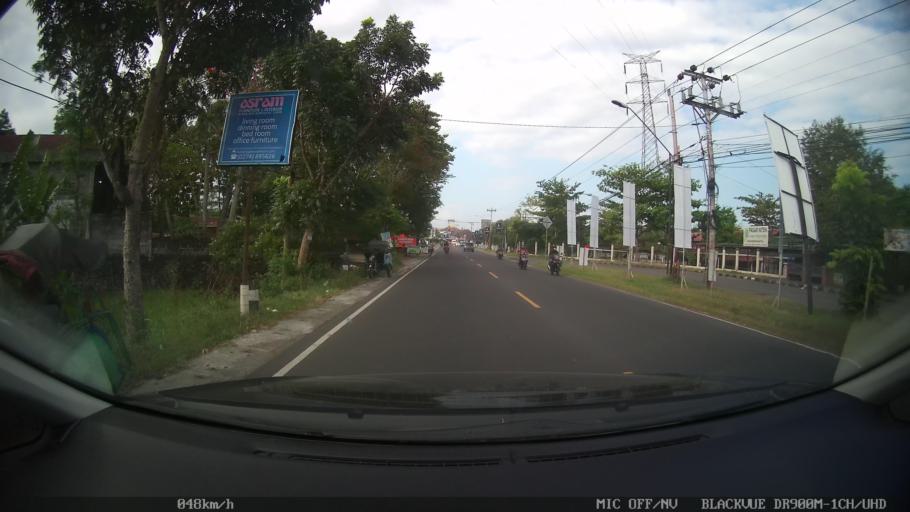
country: ID
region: Daerah Istimewa Yogyakarta
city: Kasihan
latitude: -7.8398
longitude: 110.3493
